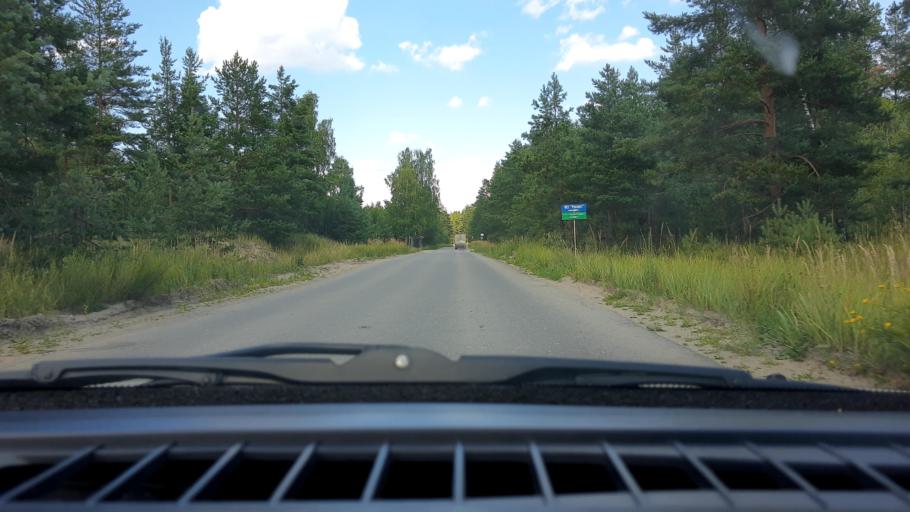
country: RU
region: Nizjnij Novgorod
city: Babino
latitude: 56.3210
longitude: 43.6301
